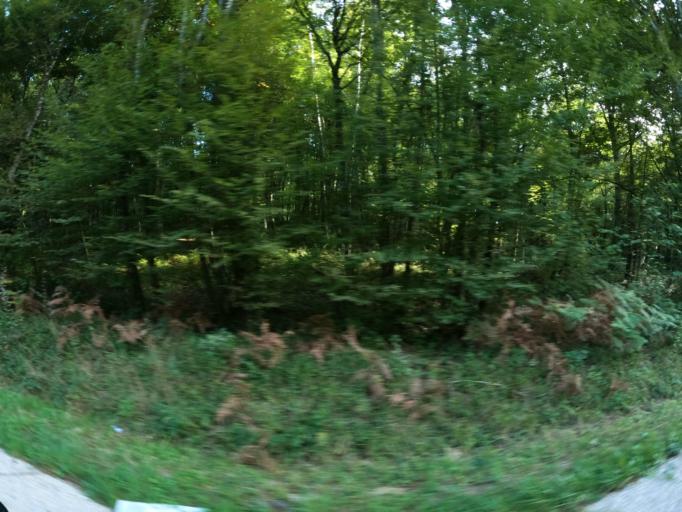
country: FR
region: Franche-Comte
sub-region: Departement du Jura
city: Montmorot
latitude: 46.7229
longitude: 5.5137
